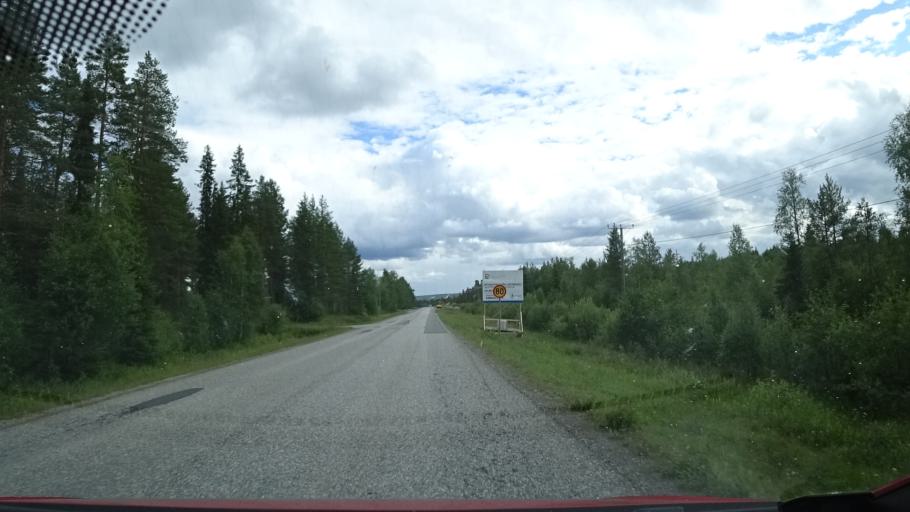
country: FI
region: Lapland
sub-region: Rovaniemi
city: Rovaniemi
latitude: 66.5447
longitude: 25.7091
